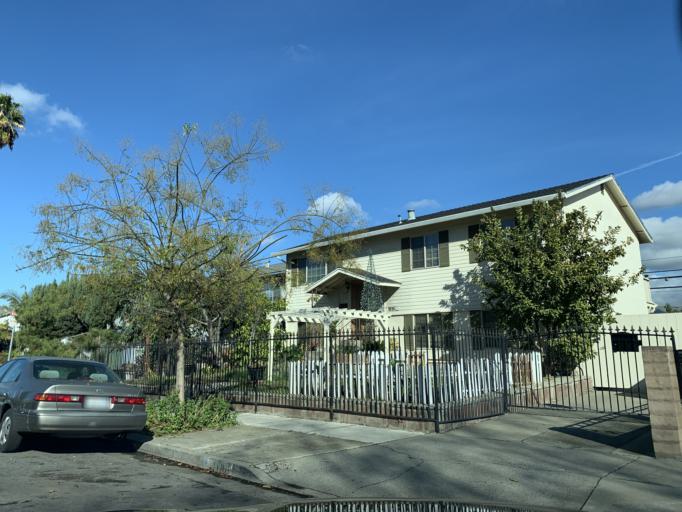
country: US
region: California
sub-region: Santa Clara County
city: Alum Rock
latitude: 37.3443
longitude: -121.8337
